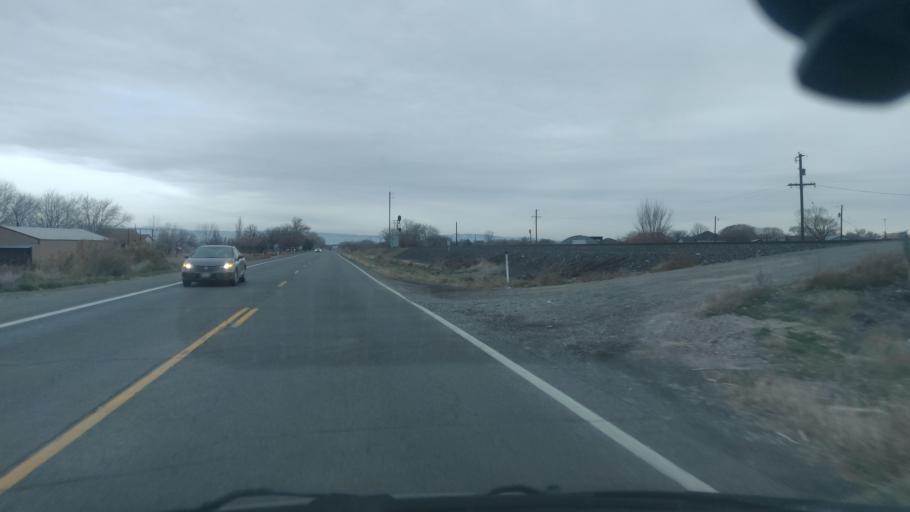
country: US
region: Colorado
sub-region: Mesa County
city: Clifton
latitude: 39.0960
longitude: -108.4148
